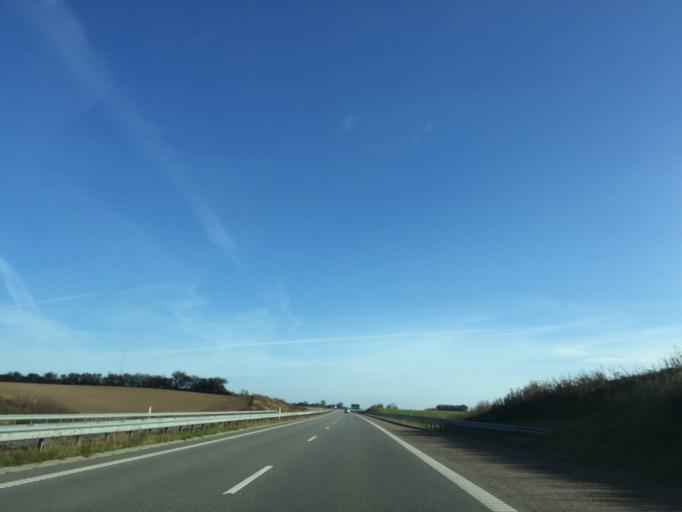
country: DK
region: South Denmark
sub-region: Sonderborg Kommune
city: Grasten
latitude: 54.9546
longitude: 9.5313
